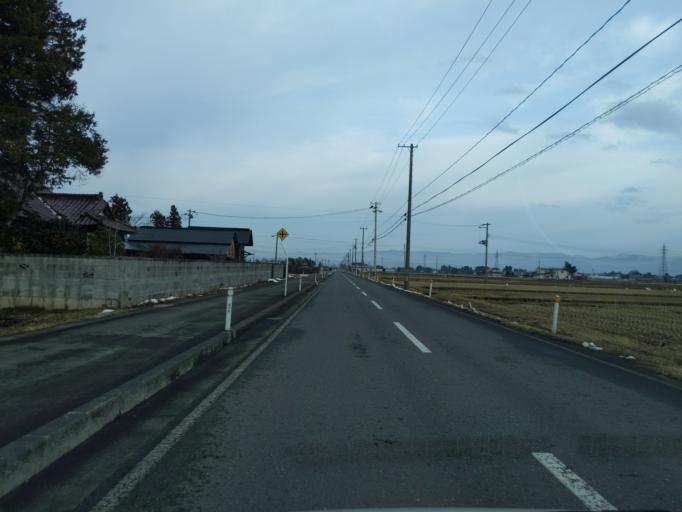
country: JP
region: Iwate
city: Mizusawa
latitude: 39.1359
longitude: 141.0952
